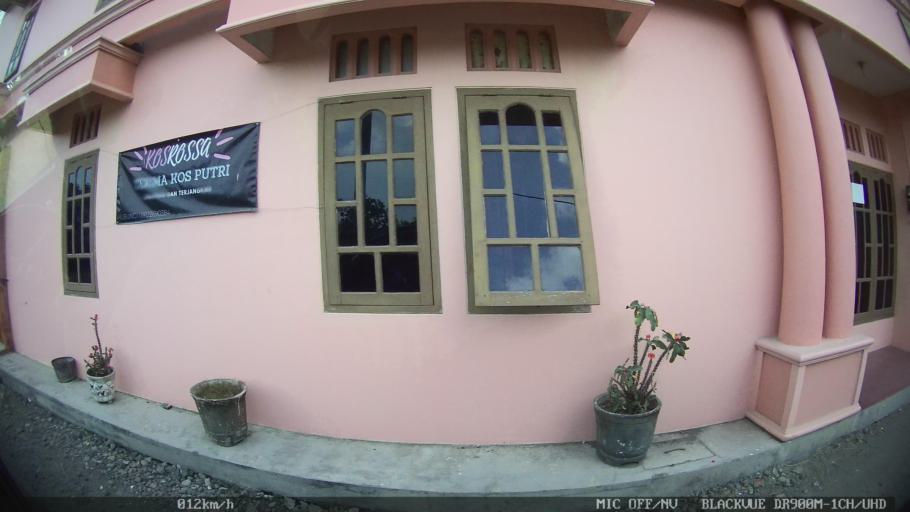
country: ID
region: Daerah Istimewa Yogyakarta
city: Kasihan
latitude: -7.8114
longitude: 110.3259
